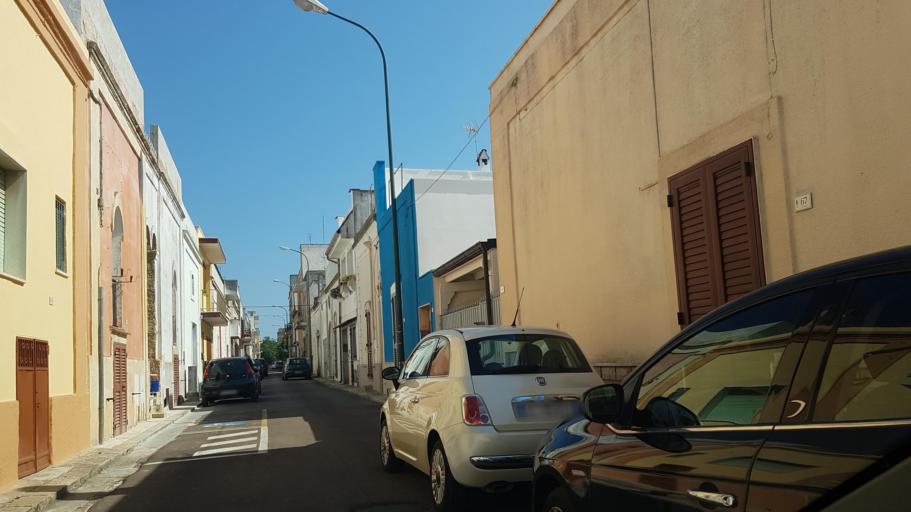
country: IT
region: Apulia
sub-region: Provincia di Lecce
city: Ugento
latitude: 39.9317
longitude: 18.1593
